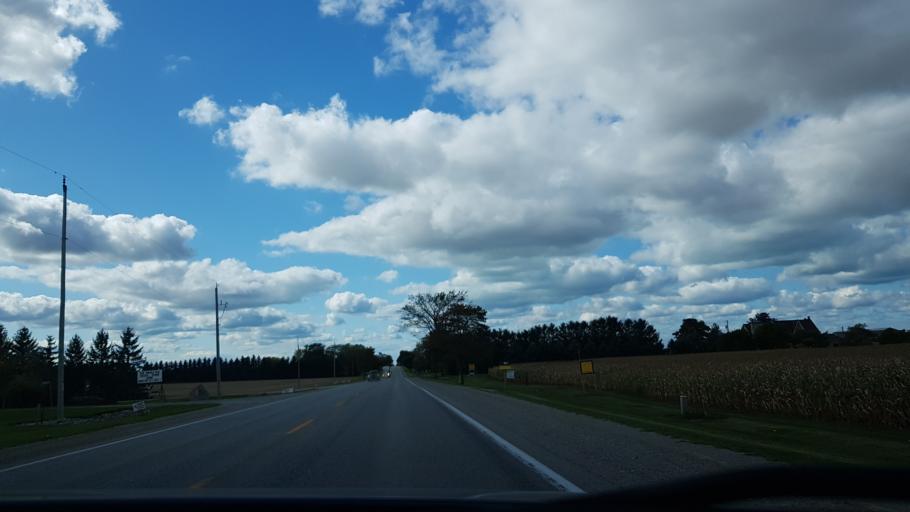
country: CA
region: Ontario
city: South Huron
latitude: 43.3478
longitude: -81.6177
